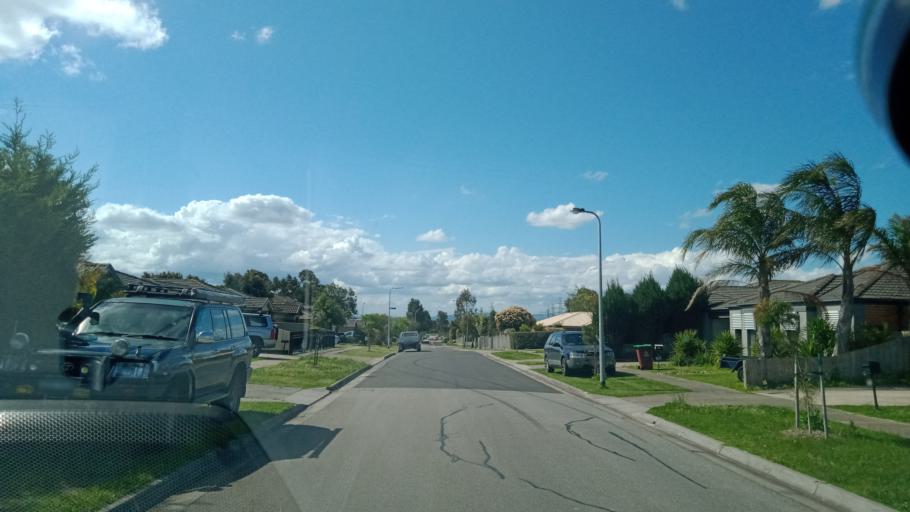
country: AU
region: Victoria
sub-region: Casey
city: Cranbourne West
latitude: -38.0969
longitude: 145.2628
